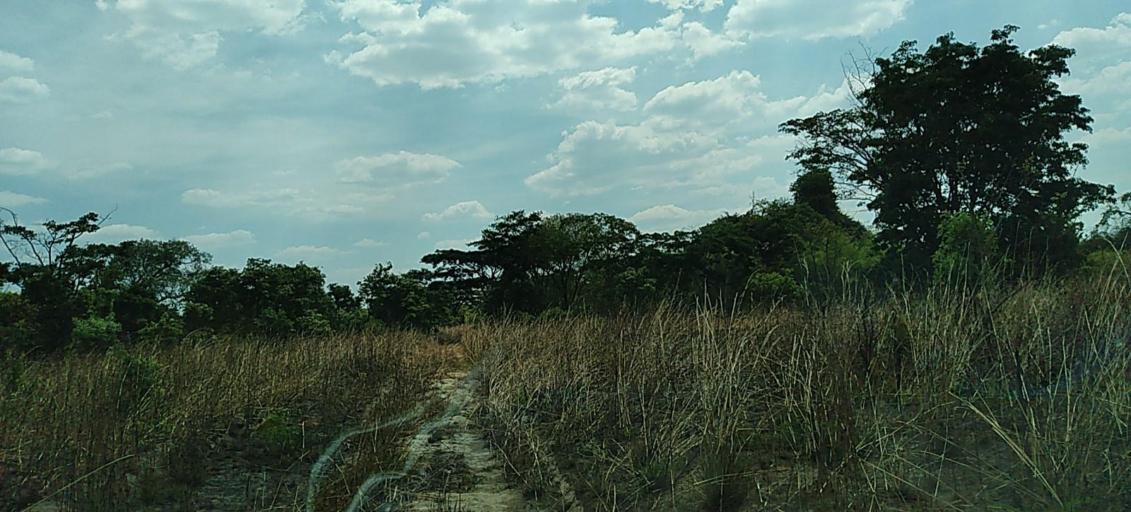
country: ZM
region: Copperbelt
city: Chililabombwe
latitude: -12.3308
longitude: 27.7661
